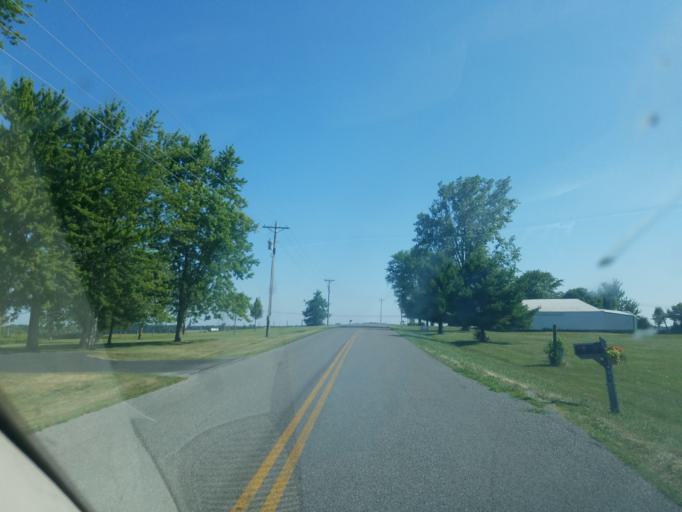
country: US
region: Ohio
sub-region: Logan County
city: Northwood
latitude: 40.4228
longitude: -83.6662
